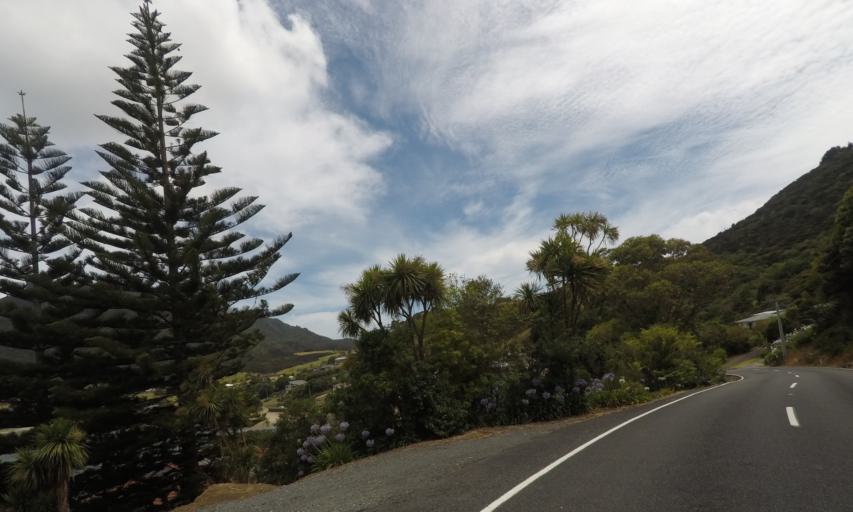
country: NZ
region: Northland
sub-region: Whangarei
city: Ruakaka
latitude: -35.8301
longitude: 174.5296
